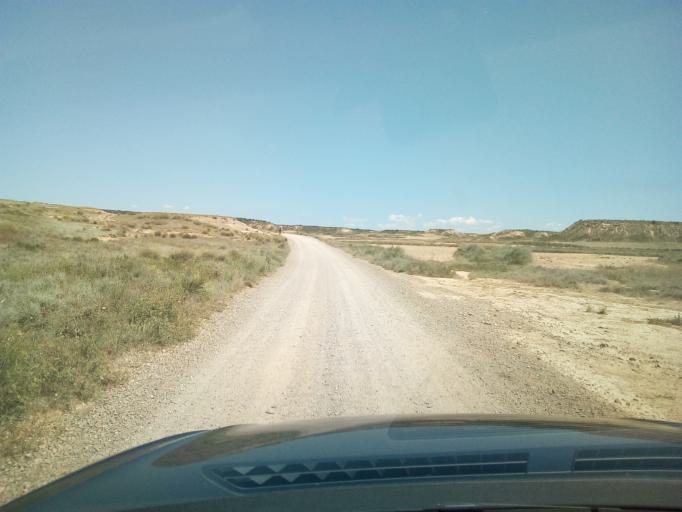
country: ES
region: Aragon
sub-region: Provincia de Zaragoza
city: Sadaba
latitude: 42.1789
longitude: -1.4082
